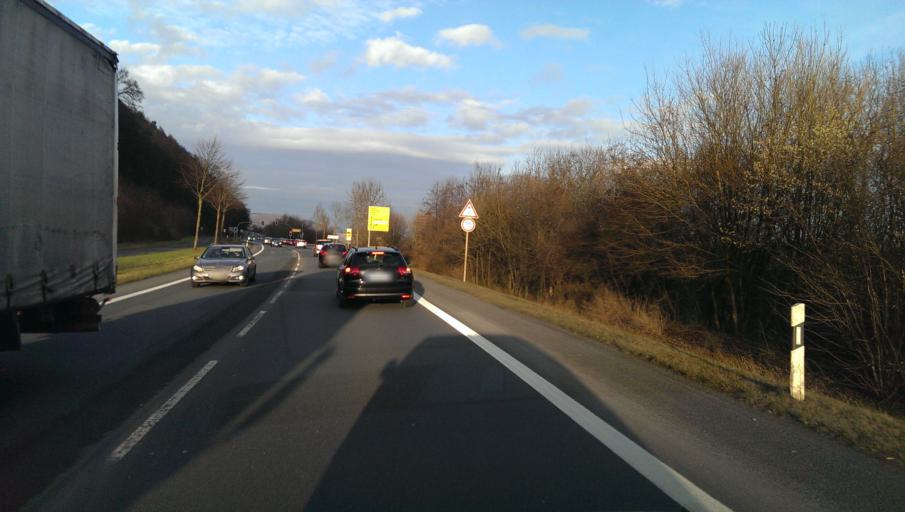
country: DE
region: North Rhine-Westphalia
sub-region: Regierungsbezirk Detmold
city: Hoexter
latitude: 51.7942
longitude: 9.3989
